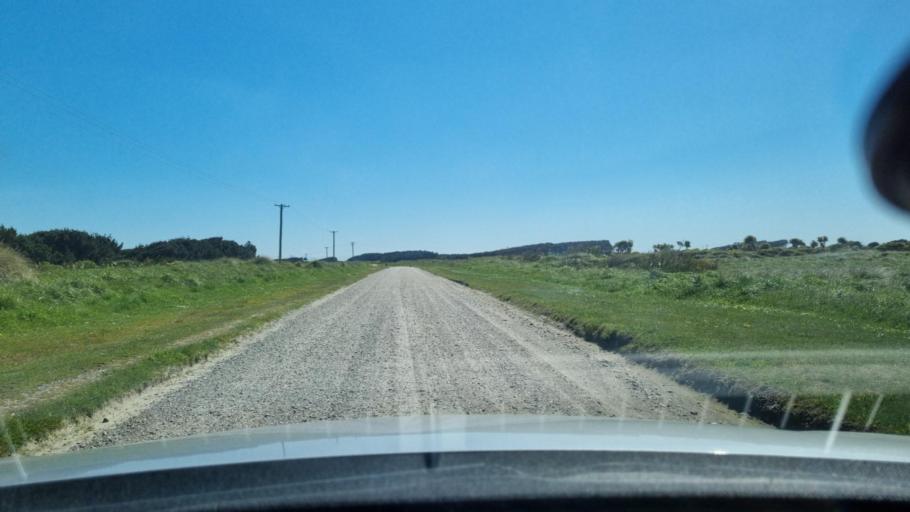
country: NZ
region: Southland
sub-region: Invercargill City
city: Invercargill
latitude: -46.4373
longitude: 168.2393
